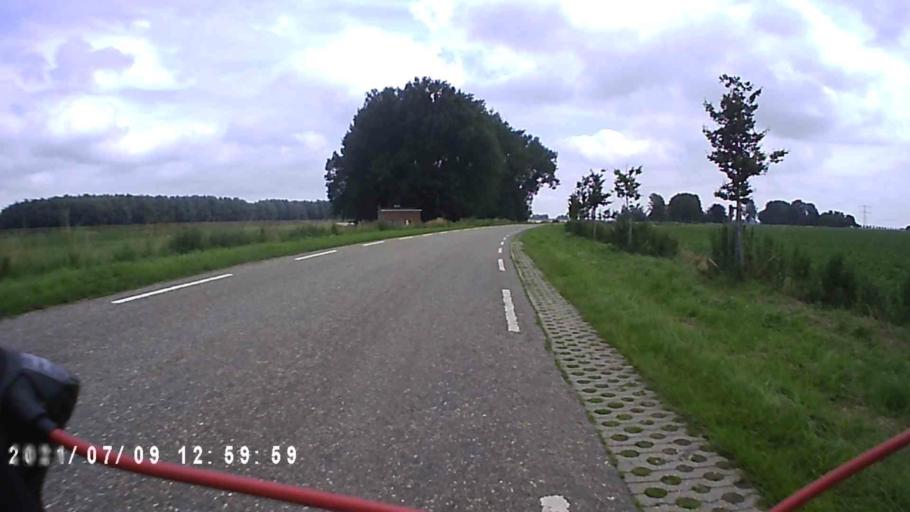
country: NL
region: Groningen
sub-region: Gemeente  Oldambt
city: Winschoten
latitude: 53.1340
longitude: 7.0688
